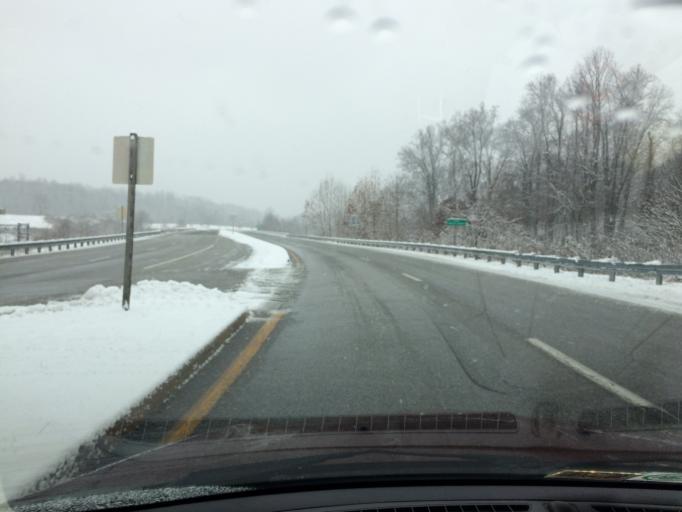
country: US
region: Virginia
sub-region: Amherst County
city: Amherst
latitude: 37.5608
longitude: -79.0657
